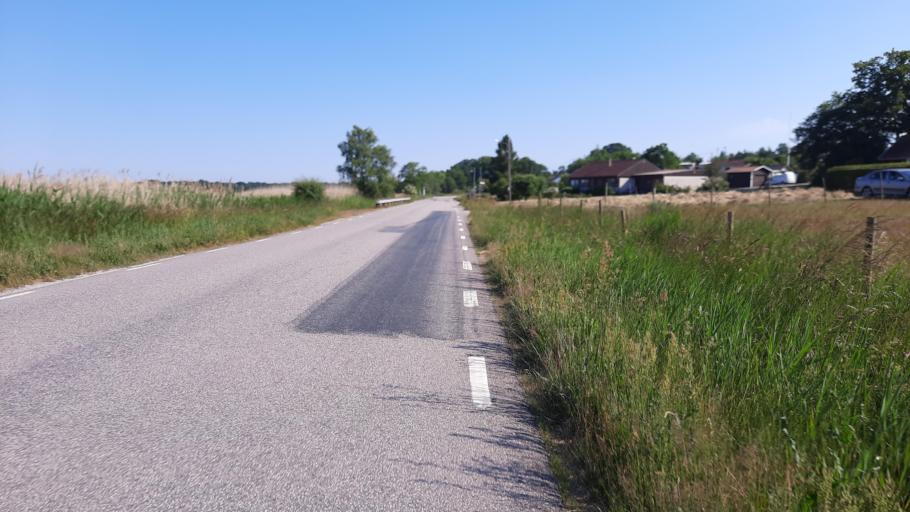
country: SE
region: Blekinge
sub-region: Karlskrona Kommun
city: Sturko
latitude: 56.1045
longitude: 15.6892
